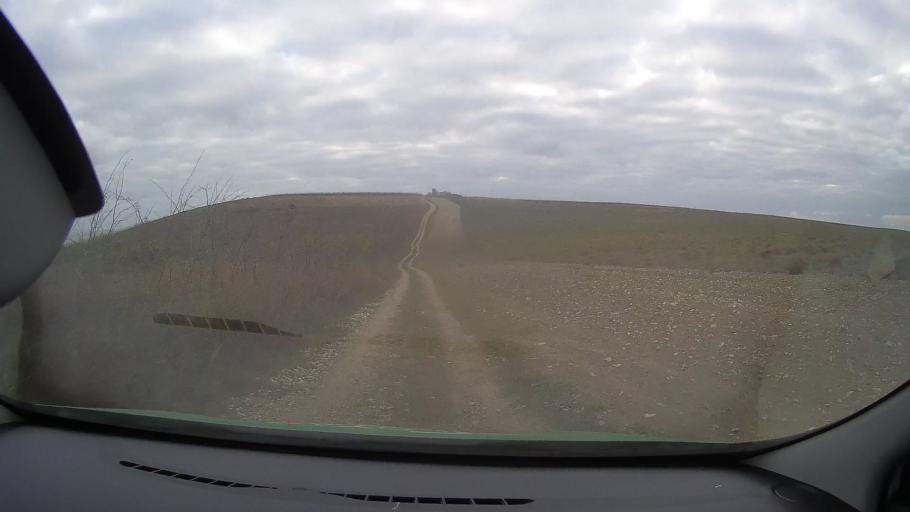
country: RO
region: Tulcea
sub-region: Comuna Jurilovca
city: Jurilovca
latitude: 44.7690
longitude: 28.9131
